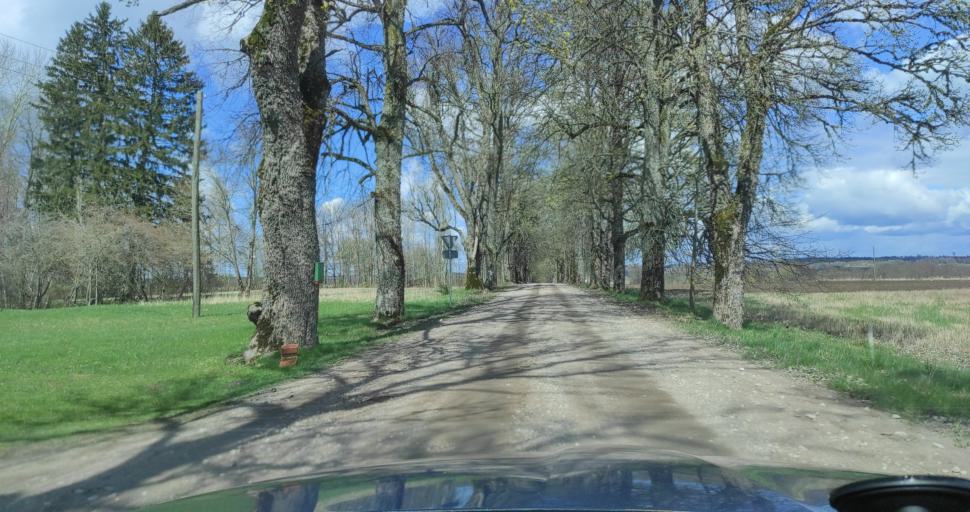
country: LV
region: Kuldigas Rajons
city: Kuldiga
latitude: 56.8580
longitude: 21.8134
